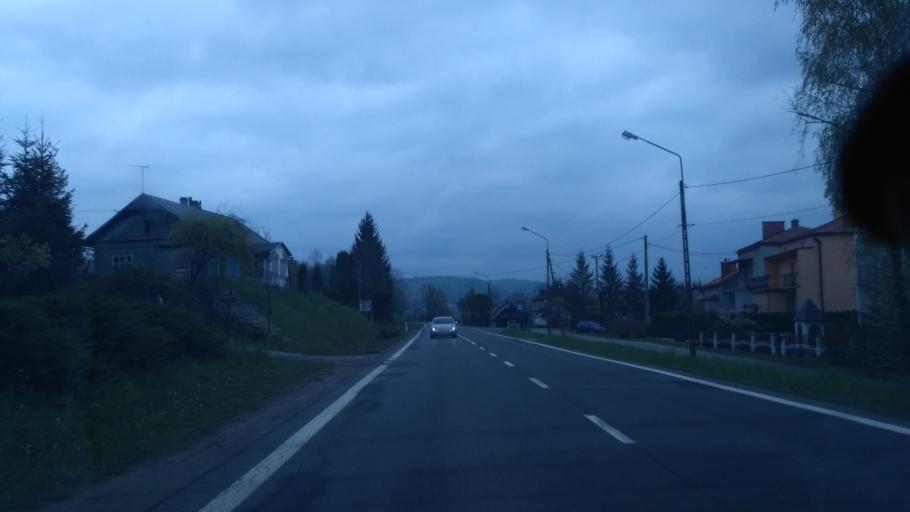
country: PL
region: Subcarpathian Voivodeship
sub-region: Powiat sanocki
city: Zagorz
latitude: 49.5426
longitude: 22.2510
